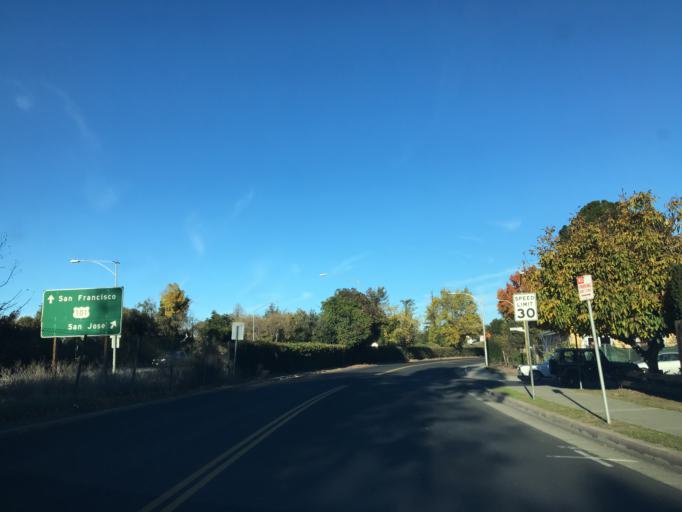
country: US
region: California
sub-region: Santa Clara County
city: Palo Alto
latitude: 37.4450
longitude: -122.1234
